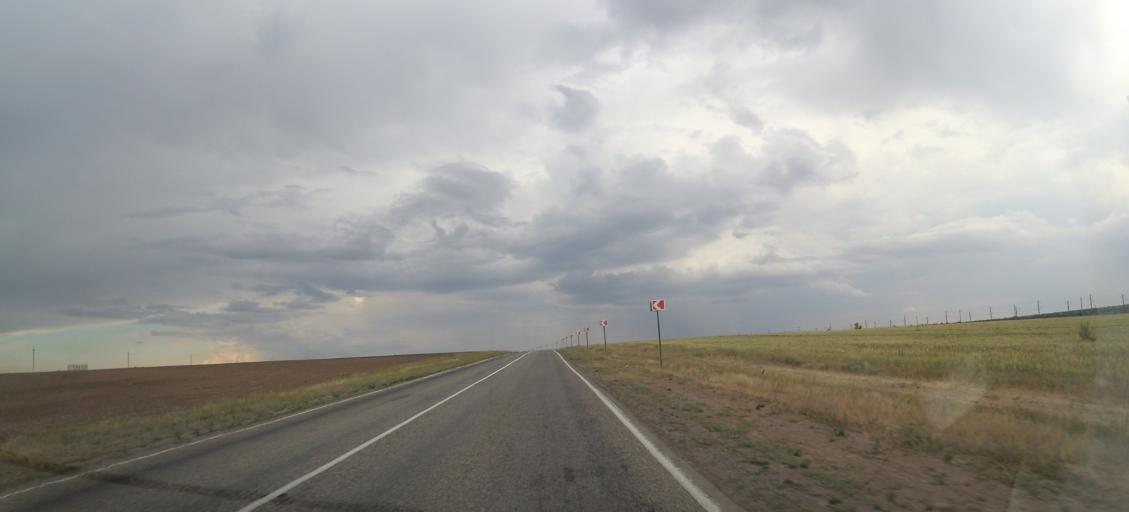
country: RU
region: Rostov
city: Dubovskoye
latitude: 47.4334
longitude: 42.7833
